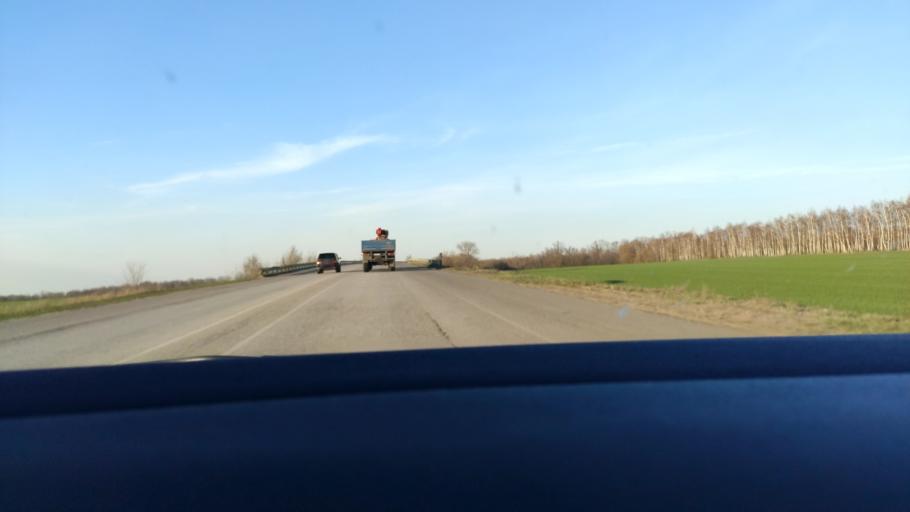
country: RU
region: Voronezj
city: Kolodeznyy
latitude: 51.4048
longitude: 39.2422
